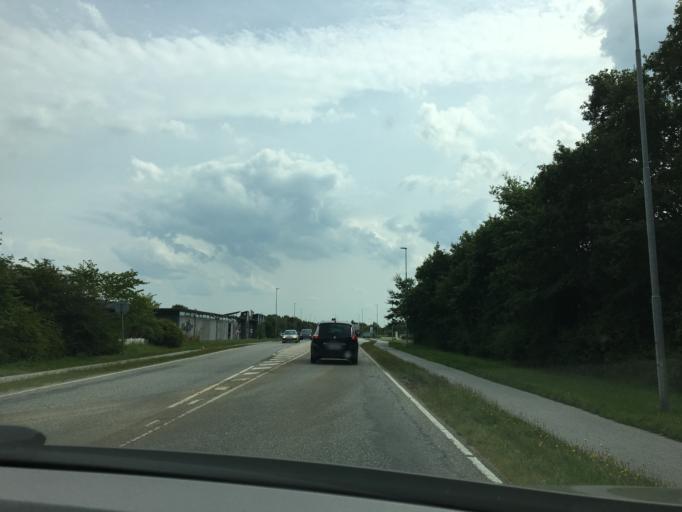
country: DK
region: Central Jutland
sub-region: Skive Kommune
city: Skive
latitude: 56.5463
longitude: 9.0293
